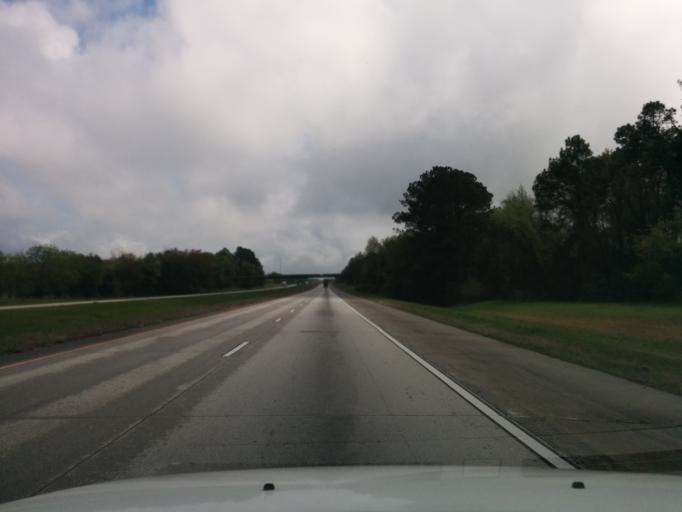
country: US
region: Georgia
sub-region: Candler County
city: Metter
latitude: 32.3551
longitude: -81.9875
